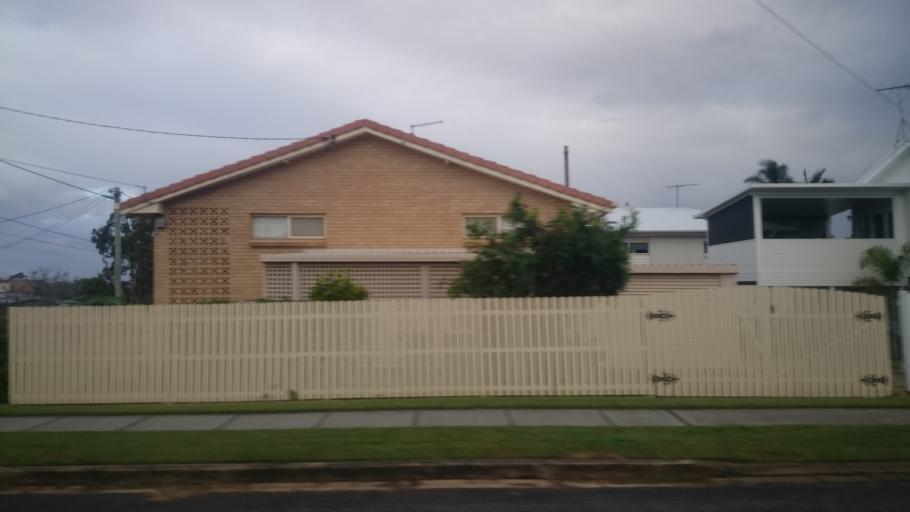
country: AU
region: Queensland
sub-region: Brisbane
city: Wynnum
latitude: -27.4513
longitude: 153.1845
